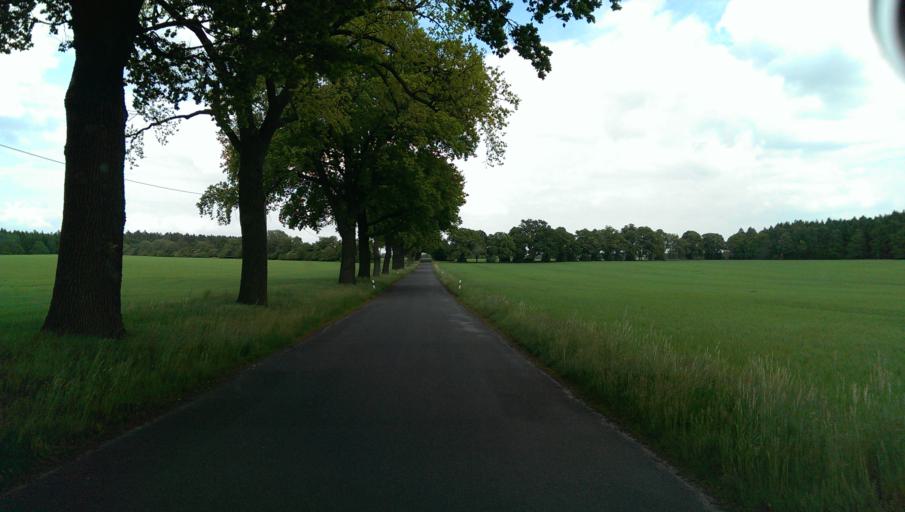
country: DE
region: Brandenburg
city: Wiesenburg
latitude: 52.1411
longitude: 12.4891
